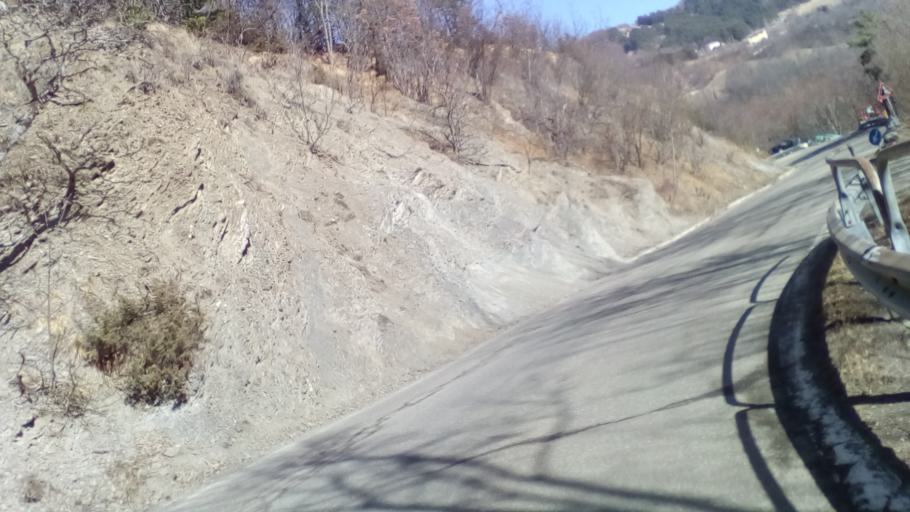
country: IT
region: Emilia-Romagna
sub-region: Provincia di Modena
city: Riolunato
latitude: 44.2498
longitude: 10.6311
